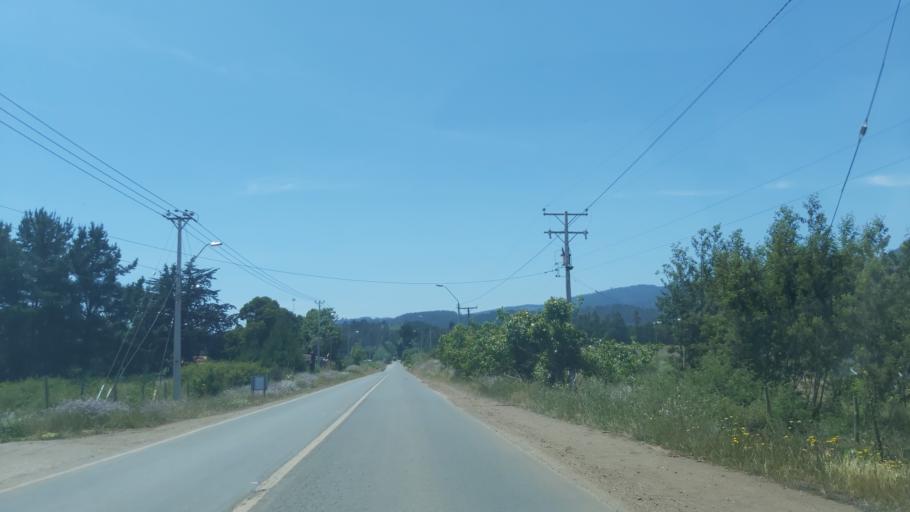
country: CL
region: Maule
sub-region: Provincia de Cauquenes
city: Cauquenes
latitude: -35.7954
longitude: -72.5493
